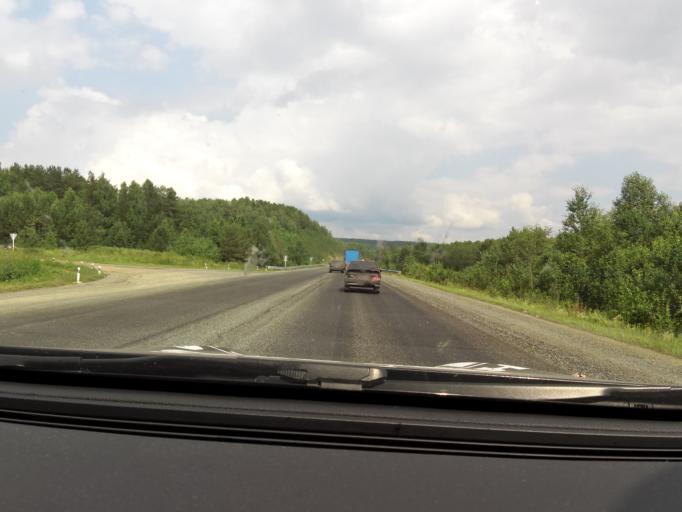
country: RU
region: Sverdlovsk
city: Ufimskiy
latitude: 56.7724
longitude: 58.2138
